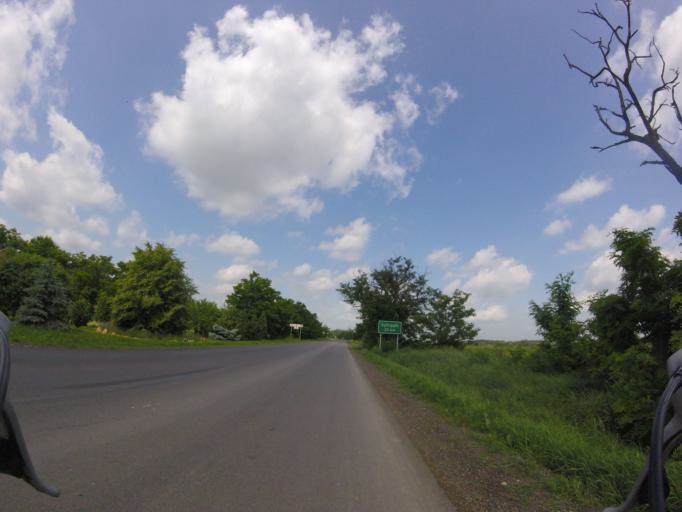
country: HU
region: Heves
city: Heves
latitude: 47.6286
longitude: 20.2347
